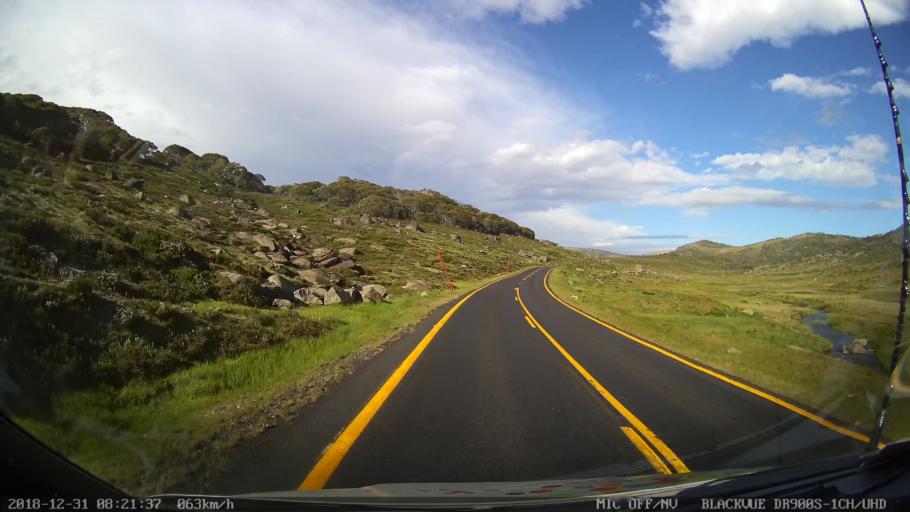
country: AU
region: New South Wales
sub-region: Snowy River
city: Jindabyne
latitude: -36.4281
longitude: 148.3667
